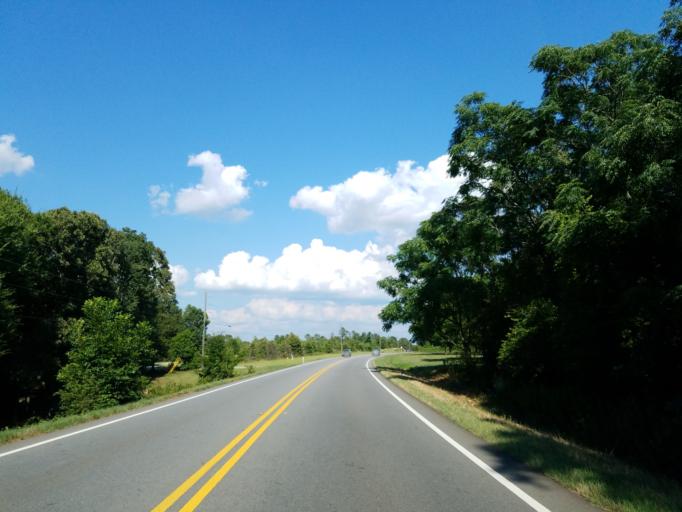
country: US
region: Georgia
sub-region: Peach County
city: Byron
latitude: 32.5536
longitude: -83.7799
